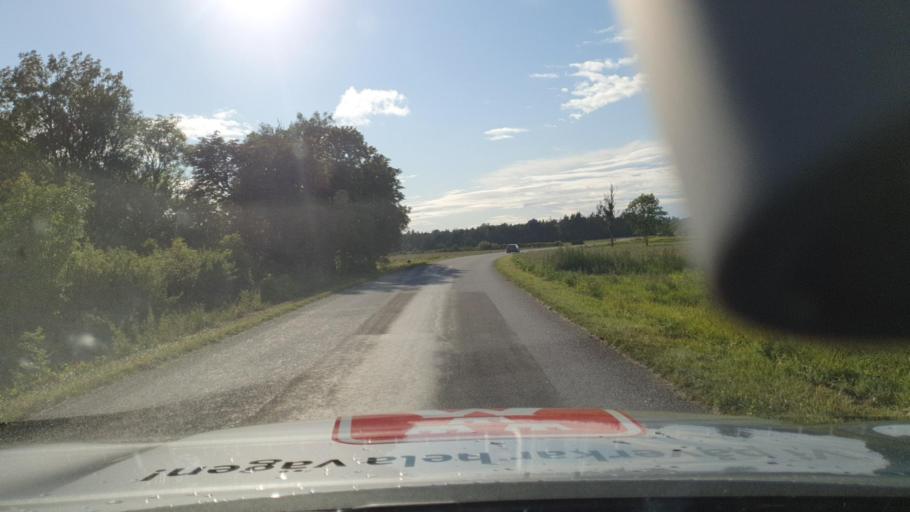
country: SE
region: Gotland
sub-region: Gotland
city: Slite
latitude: 57.5408
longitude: 18.6245
